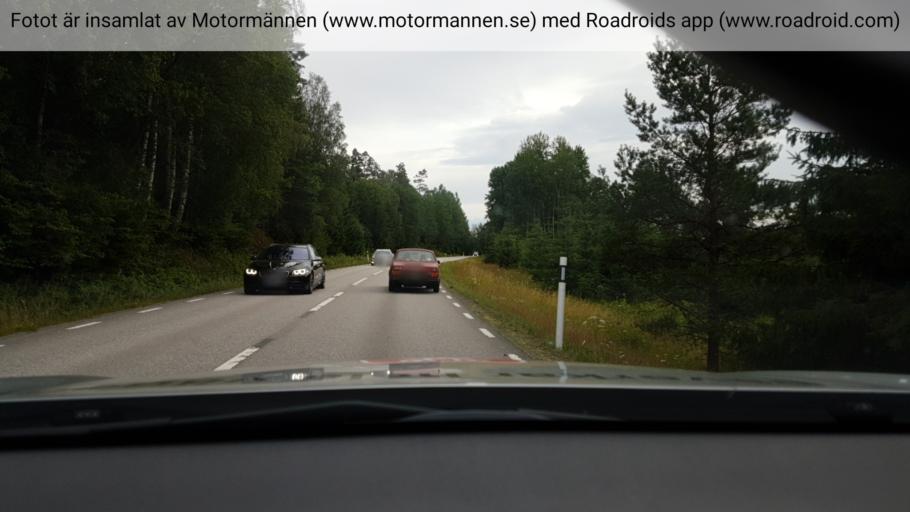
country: SE
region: Vaestra Goetaland
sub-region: Bengtsfors Kommun
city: Dals Langed
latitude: 58.9083
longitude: 12.2199
